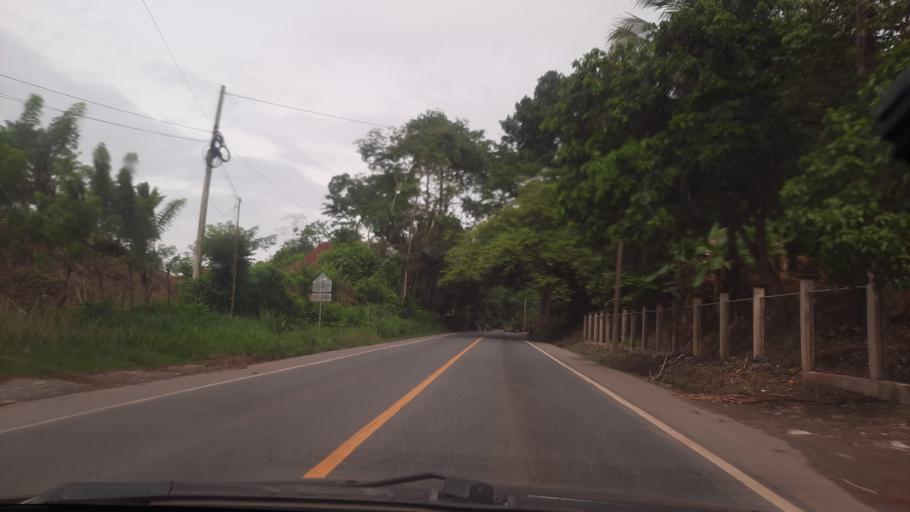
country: GT
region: Izabal
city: Morales
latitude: 15.5137
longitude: -88.8010
